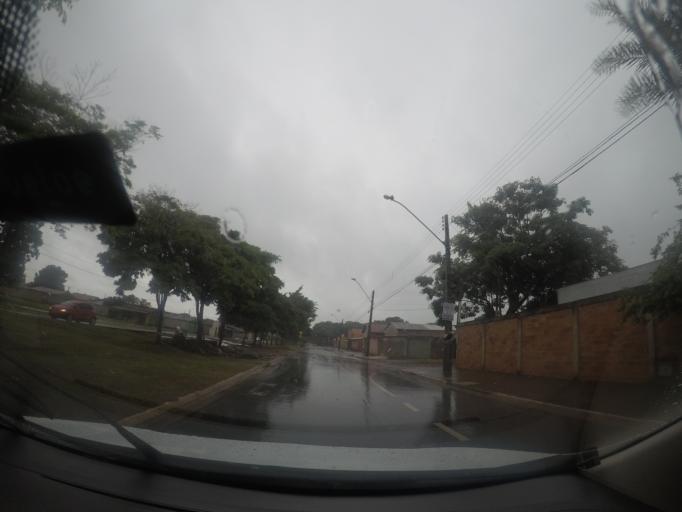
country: BR
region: Goias
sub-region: Goiania
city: Goiania
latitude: -16.5995
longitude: -49.3396
